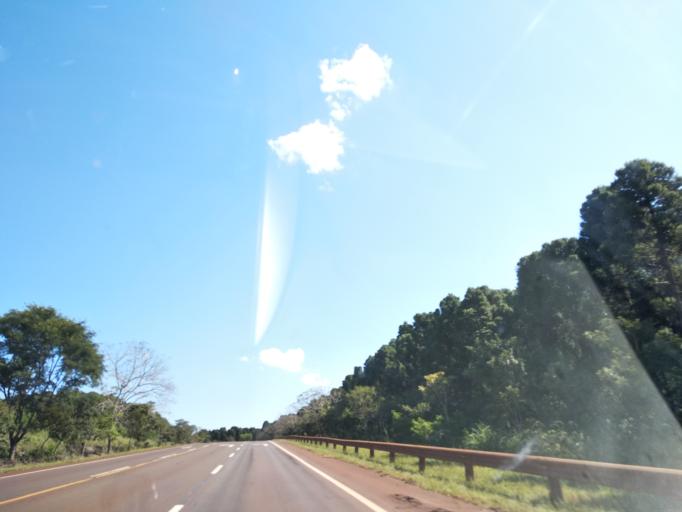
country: AR
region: Misiones
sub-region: Departamento de Montecarlo
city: Montecarlo
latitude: -26.5363
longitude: -54.7225
